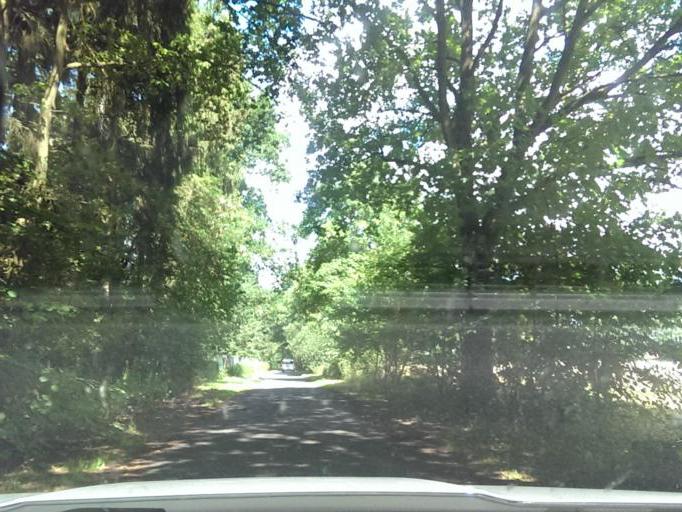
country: DE
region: Lower Saxony
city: Elze
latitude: 52.5386
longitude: 9.7216
